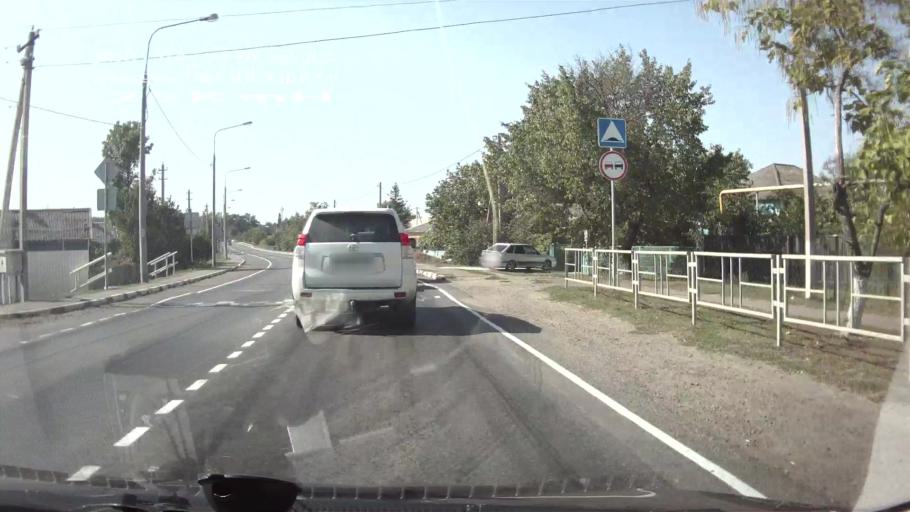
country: RU
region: Krasnodarskiy
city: Novopokrovskaya
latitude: 45.9621
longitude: 40.7109
